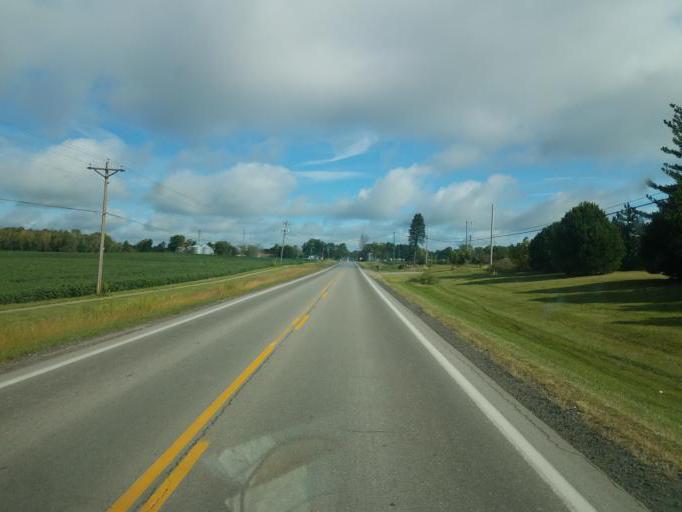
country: US
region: Ohio
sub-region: Wayne County
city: West Salem
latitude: 40.9627
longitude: -82.1096
